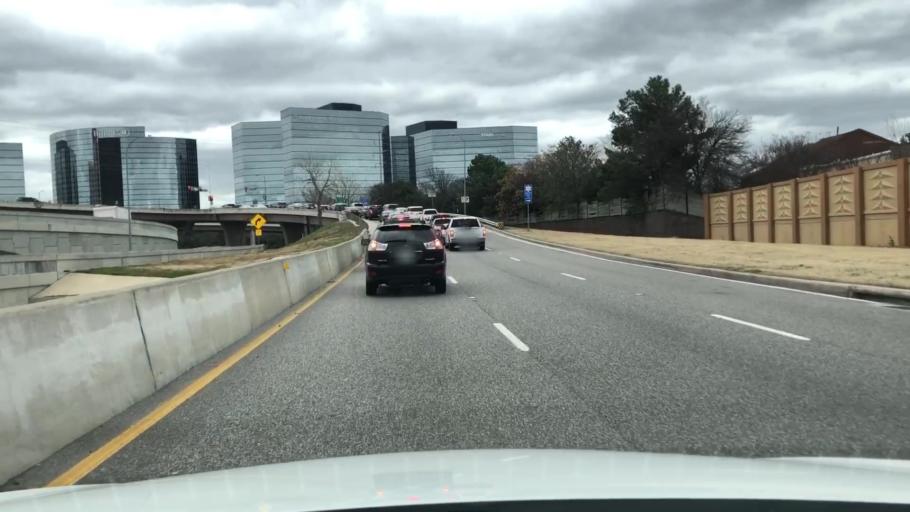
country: US
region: Texas
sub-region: Dallas County
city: Addison
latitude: 32.9238
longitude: -96.8230
